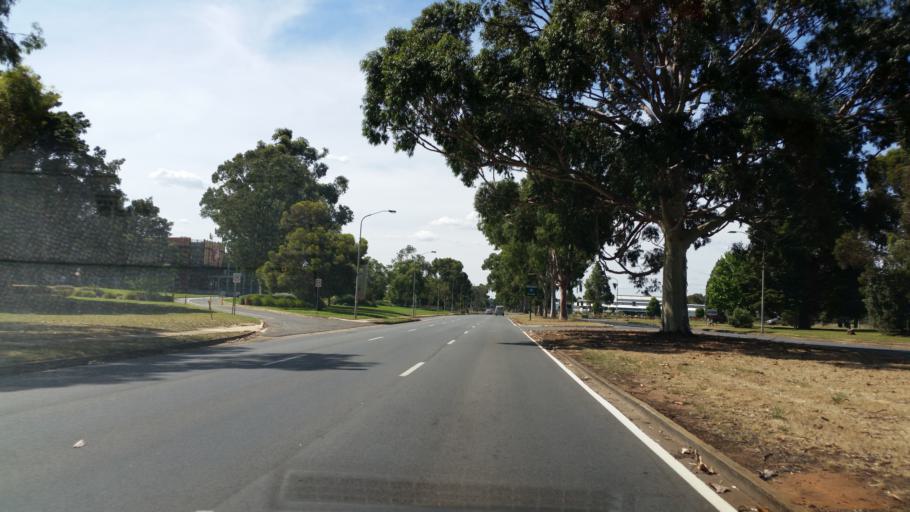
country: AU
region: South Australia
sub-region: Salisbury
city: Salisbury
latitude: -34.7472
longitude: 138.6574
